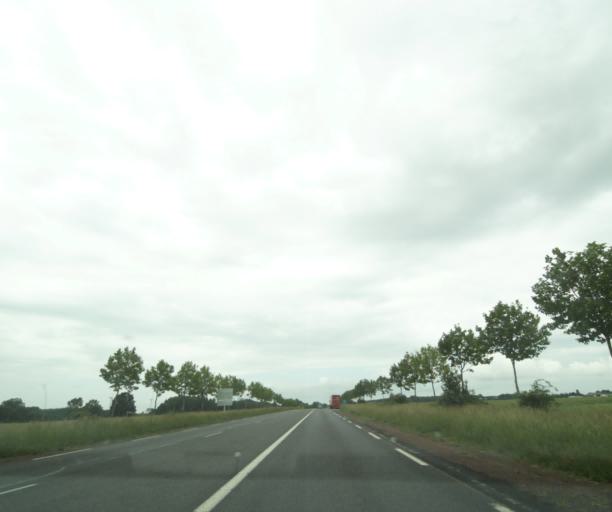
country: FR
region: Poitou-Charentes
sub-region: Departement des Deux-Sevres
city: Saint-Varent
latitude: 46.8419
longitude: -0.2084
